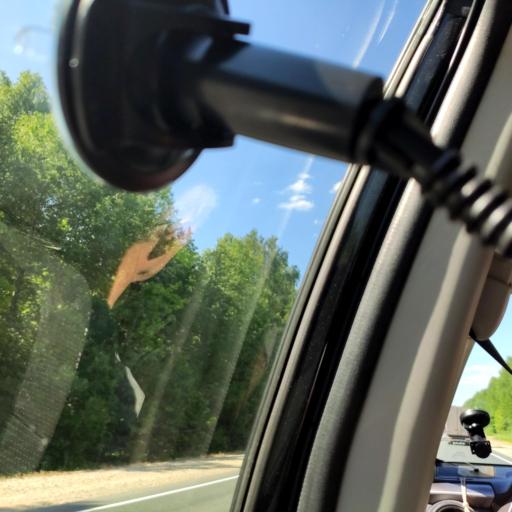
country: RU
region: Mariy-El
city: Suslonger
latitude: 56.2286
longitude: 48.2338
